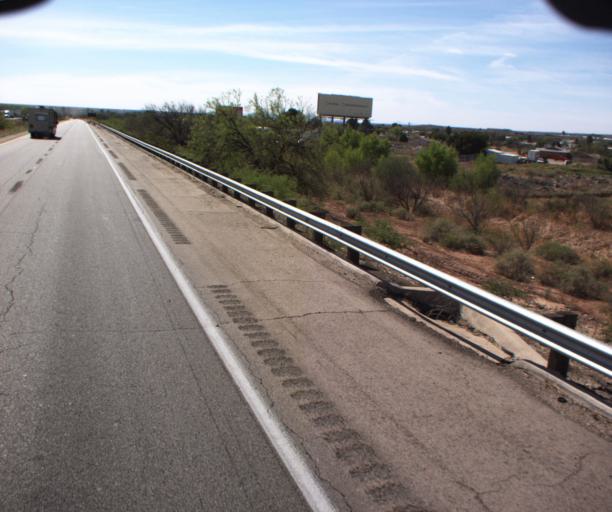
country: US
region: Arizona
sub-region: Cochise County
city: Benson
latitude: 31.9735
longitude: -110.2867
